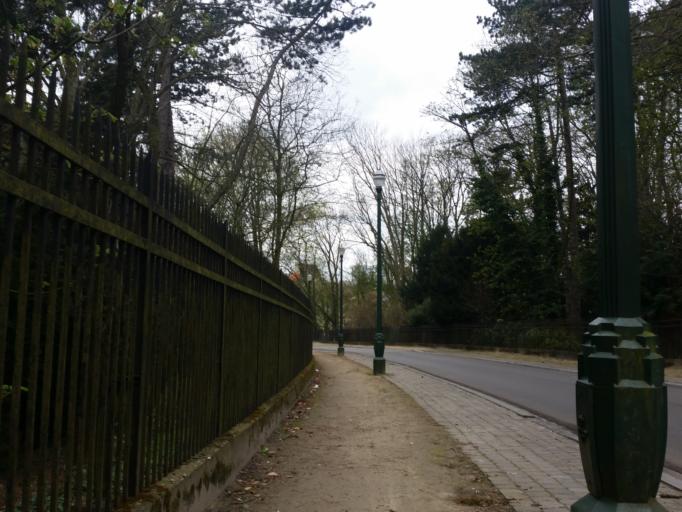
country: BE
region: Brussels Capital
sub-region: Bruxelles-Capitale
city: Brussels
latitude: 50.8867
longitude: 4.3464
